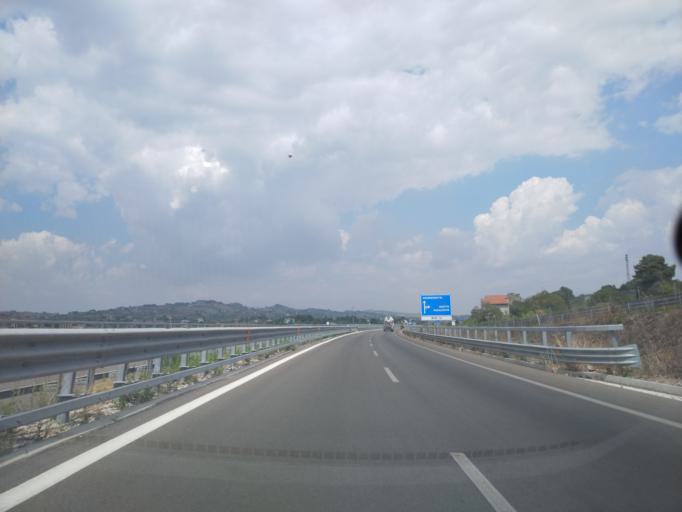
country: IT
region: Sicily
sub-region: Agrigento
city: Grotte
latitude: 37.3696
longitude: 13.7079
